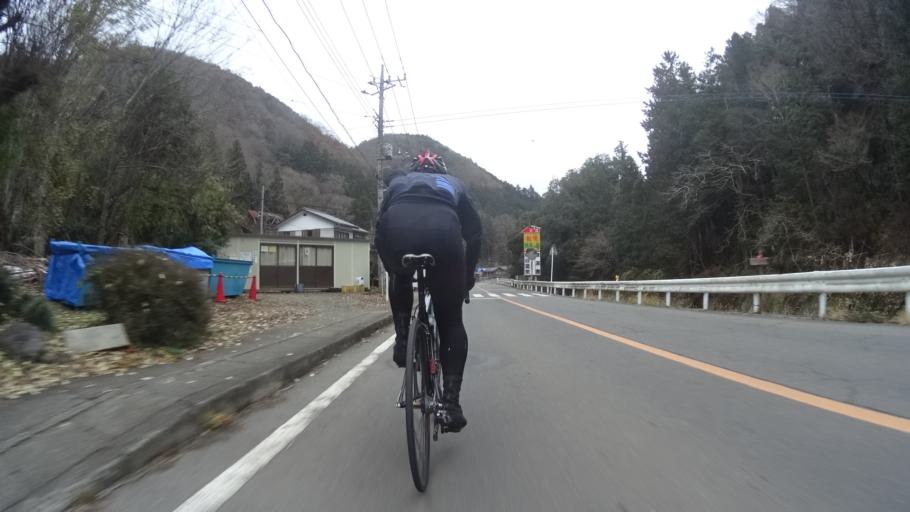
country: JP
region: Yamanashi
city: Uenohara
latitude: 35.6297
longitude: 139.1472
